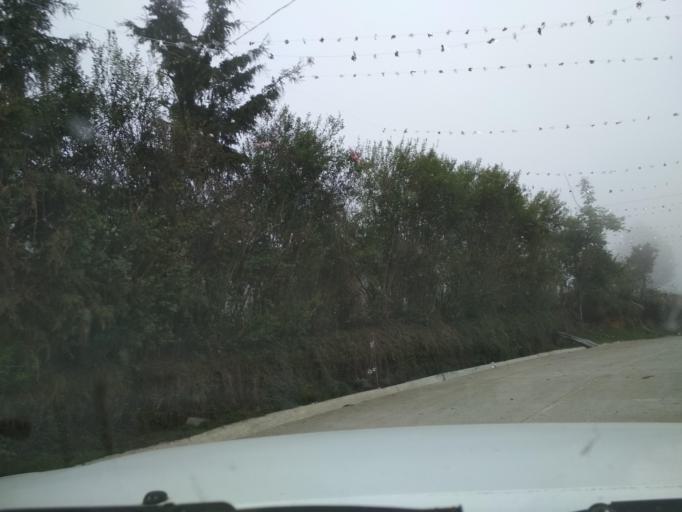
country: MX
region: Veracruz
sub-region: La Perla
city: Chilapa
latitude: 18.9831
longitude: -97.1978
